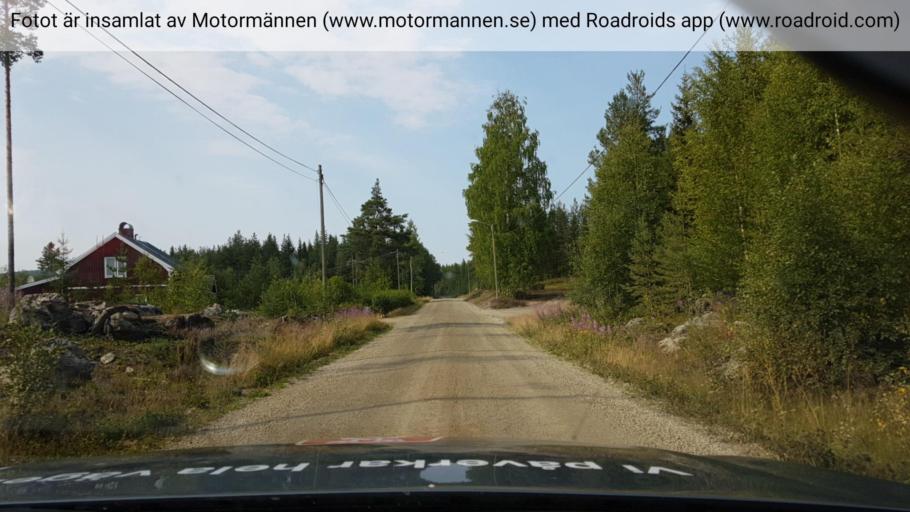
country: SE
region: Jaemtland
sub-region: Braecke Kommun
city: Braecke
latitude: 62.4631
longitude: 14.9194
